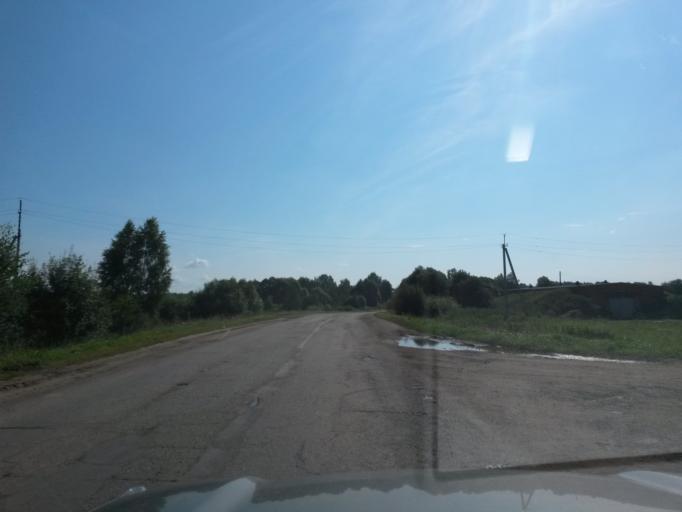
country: RU
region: Jaroslavl
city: Gavrilov-Yam
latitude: 57.3053
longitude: 39.9842
